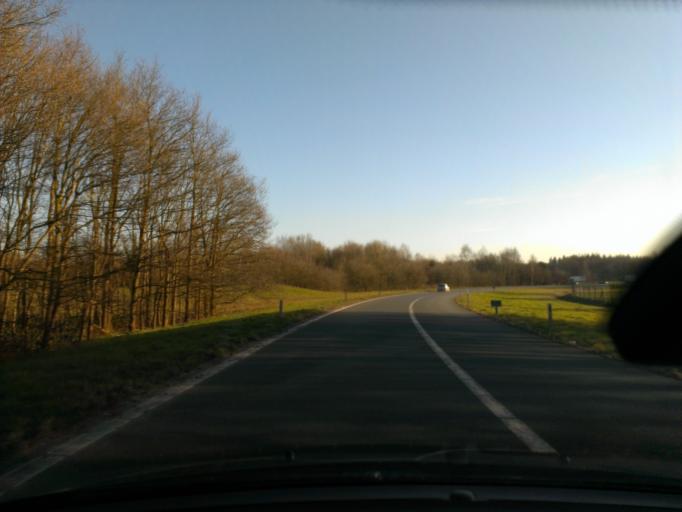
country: NL
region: Overijssel
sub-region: Gemeente Almelo
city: Almelo
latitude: 52.3124
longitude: 6.6918
